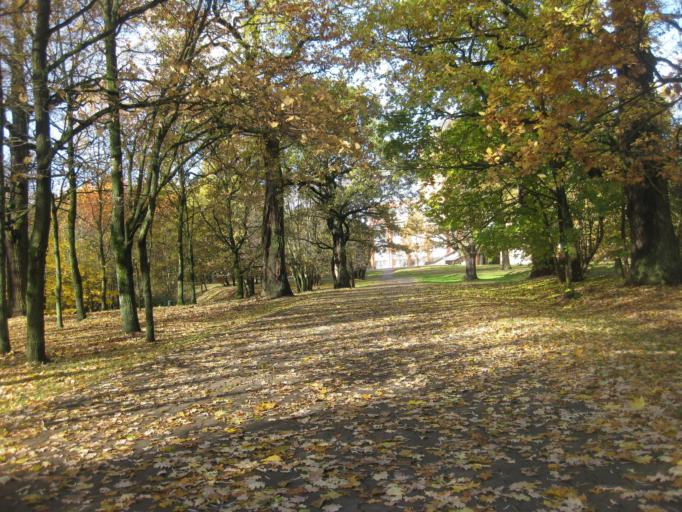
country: LT
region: Kauno apskritis
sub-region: Kaunas
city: Kaunas
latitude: 54.8990
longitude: 23.9318
